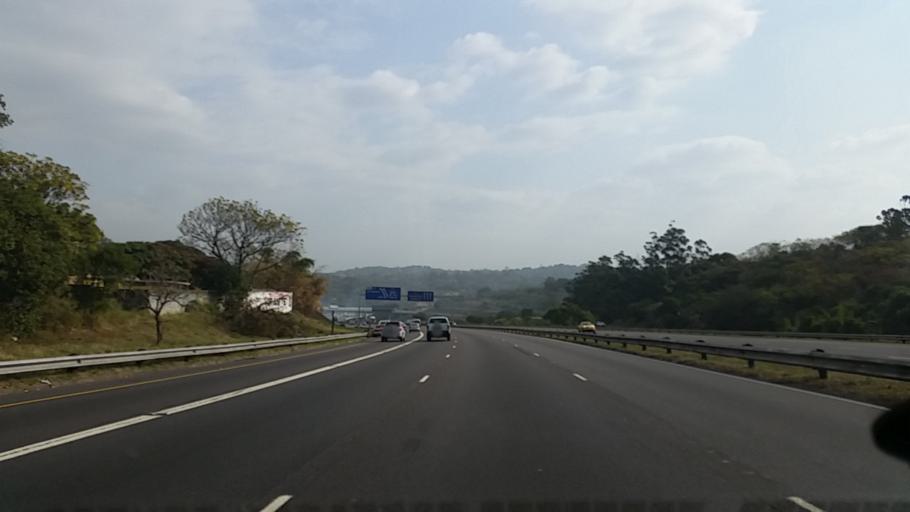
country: ZA
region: KwaZulu-Natal
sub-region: eThekwini Metropolitan Municipality
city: Berea
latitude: -29.8391
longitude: 30.9646
